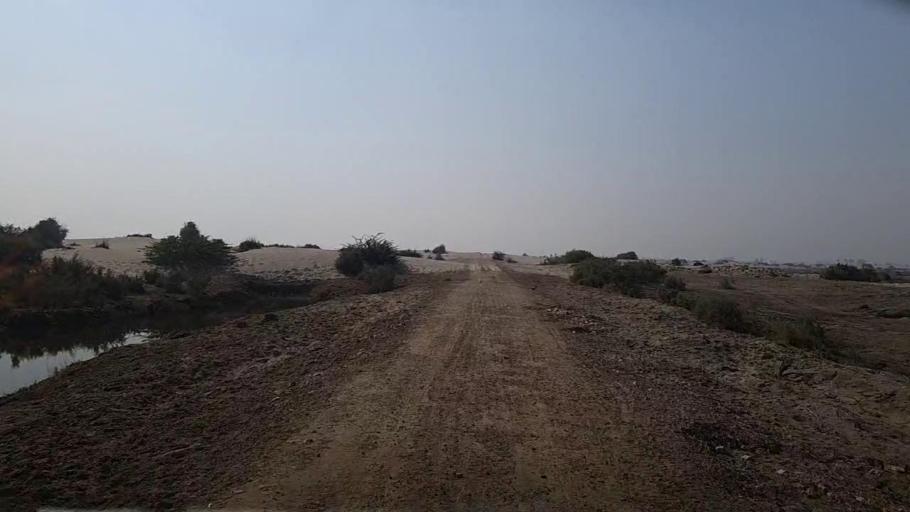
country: PK
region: Sindh
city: Bozdar
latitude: 27.2251
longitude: 68.5877
